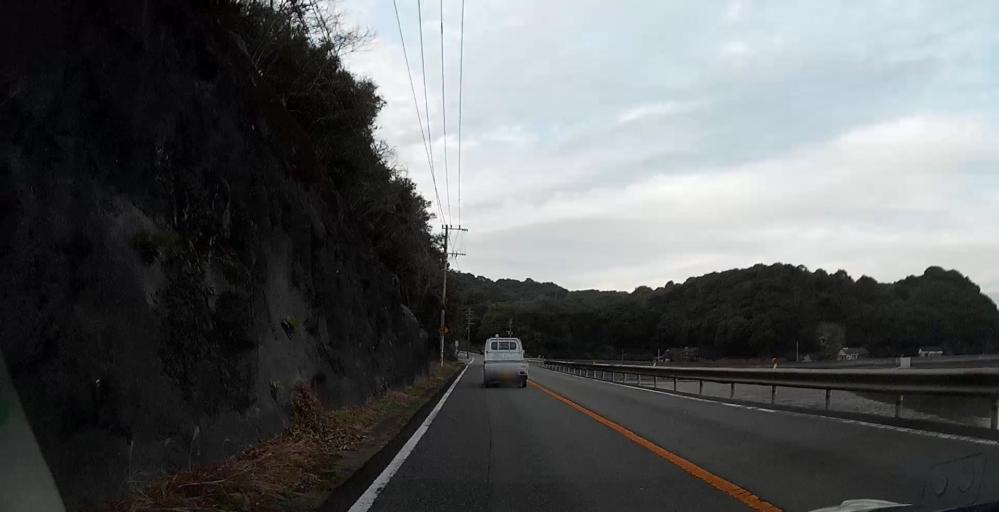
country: JP
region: Kumamoto
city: Hondo
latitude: 32.5037
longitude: 130.3902
